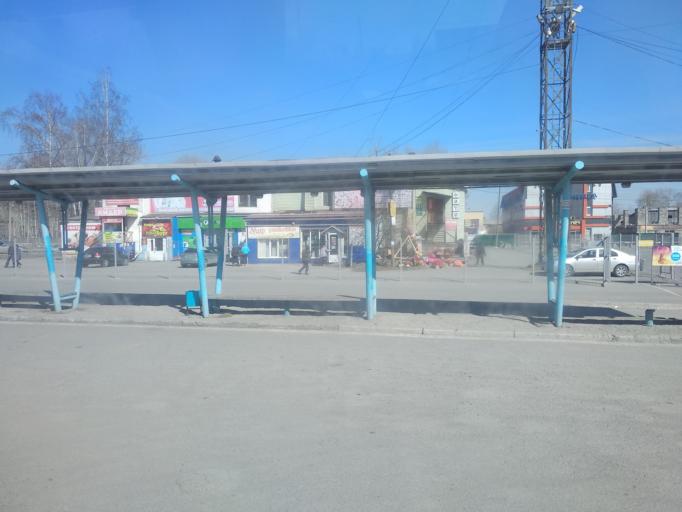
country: RU
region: Sverdlovsk
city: Serov
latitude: 59.5980
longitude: 60.5919
